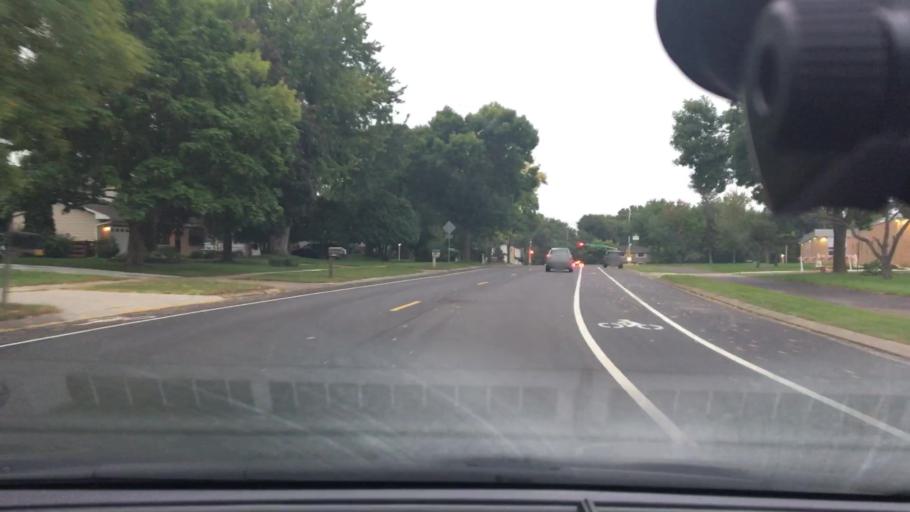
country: US
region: Minnesota
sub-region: Hennepin County
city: New Hope
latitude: 45.0092
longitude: -93.3904
